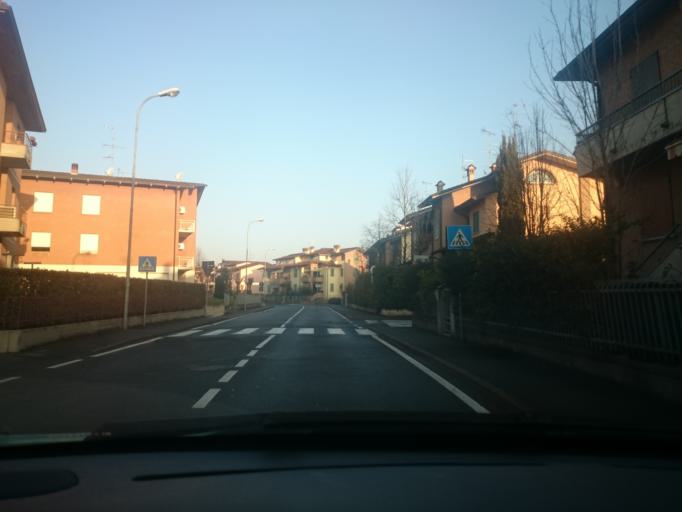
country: IT
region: Emilia-Romagna
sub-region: Provincia di Reggio Emilia
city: Fellegara
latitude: 44.6052
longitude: 10.6963
